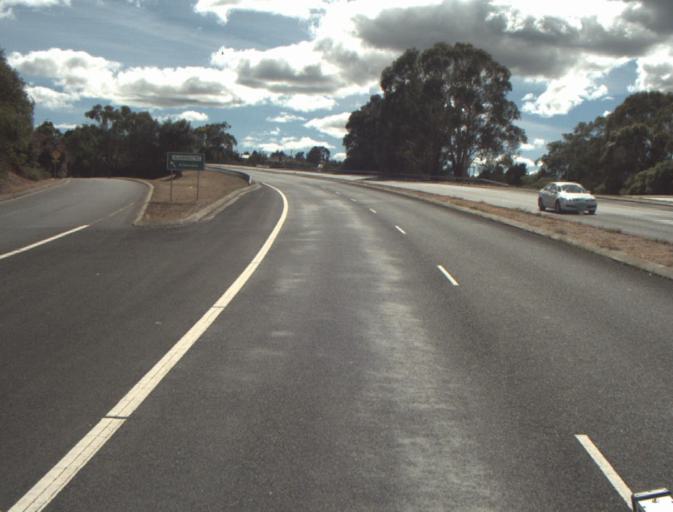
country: AU
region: Tasmania
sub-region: Launceston
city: Newnham
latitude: -41.3961
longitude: 147.1231
